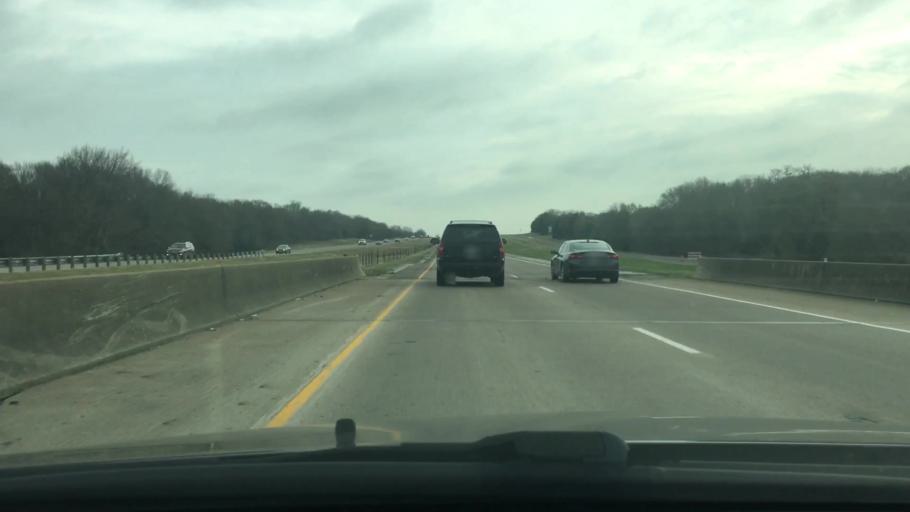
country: US
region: Texas
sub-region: Freestone County
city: Fairfield
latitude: 31.6467
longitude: -96.1596
